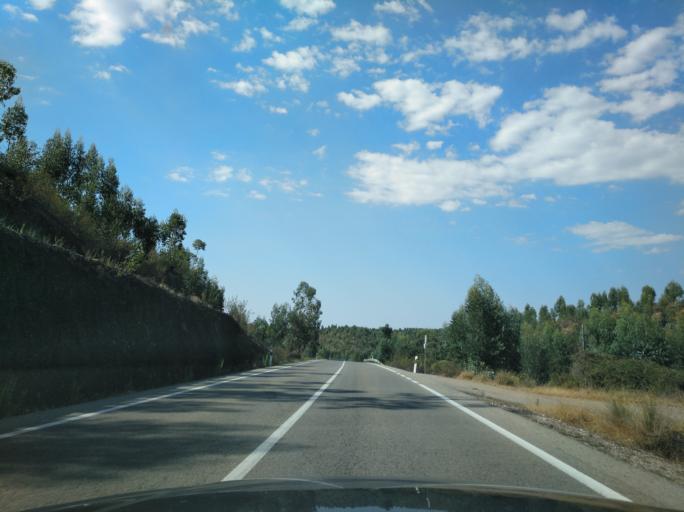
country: ES
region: Andalusia
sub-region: Provincia de Huelva
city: Santa Barbara de Casa
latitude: 37.8218
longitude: -7.2094
